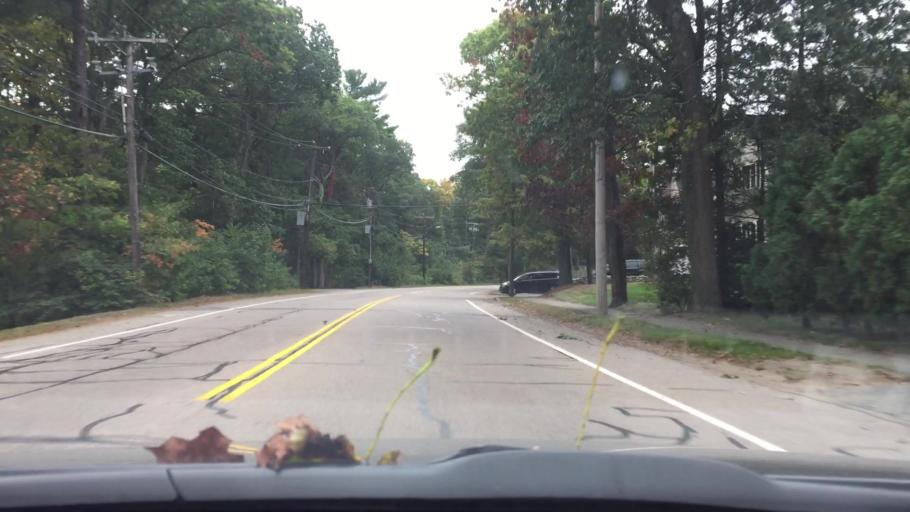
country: US
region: Massachusetts
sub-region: Norfolk County
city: Needham
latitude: 42.2814
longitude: -71.2049
